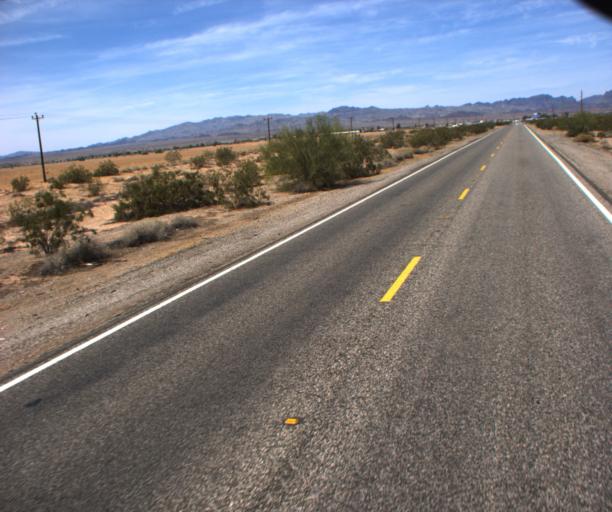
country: US
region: Arizona
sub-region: La Paz County
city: Parker
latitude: 34.1193
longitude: -114.2788
